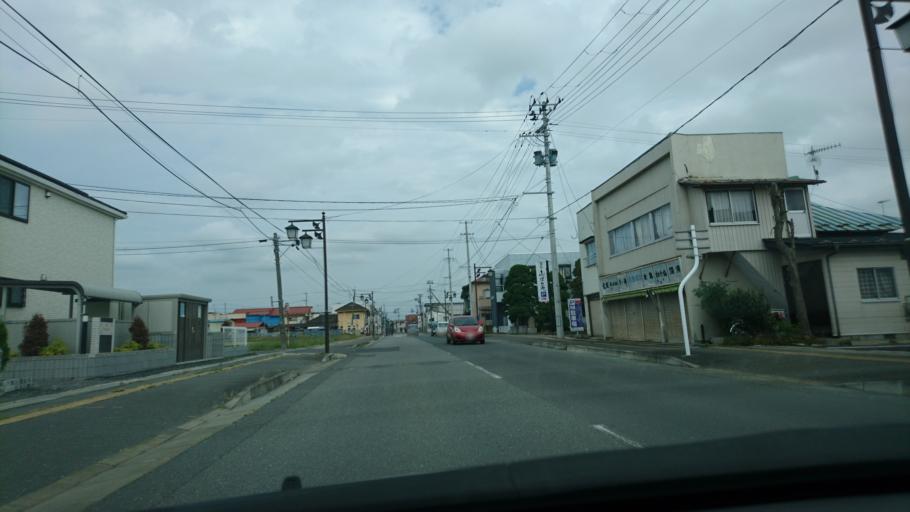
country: JP
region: Miyagi
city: Furukawa
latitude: 38.7320
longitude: 141.0262
